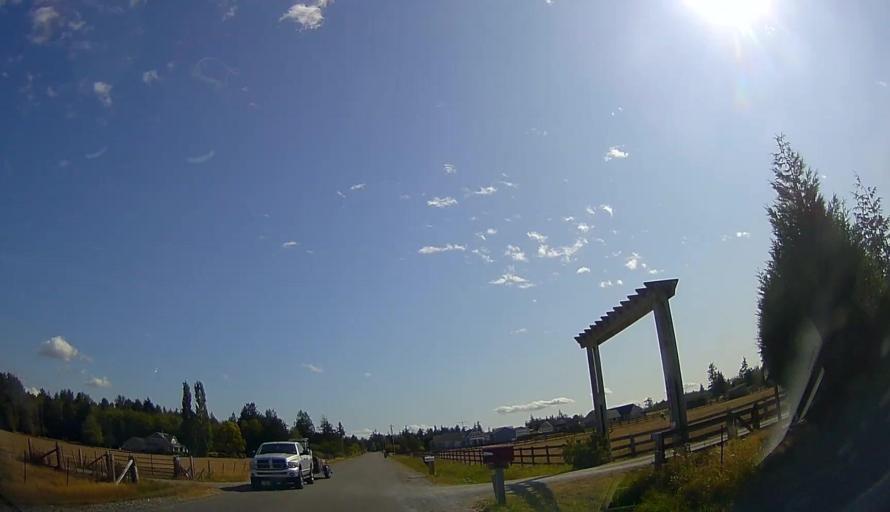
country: US
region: Washington
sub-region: Skagit County
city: Burlington
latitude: 48.4995
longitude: -122.4611
